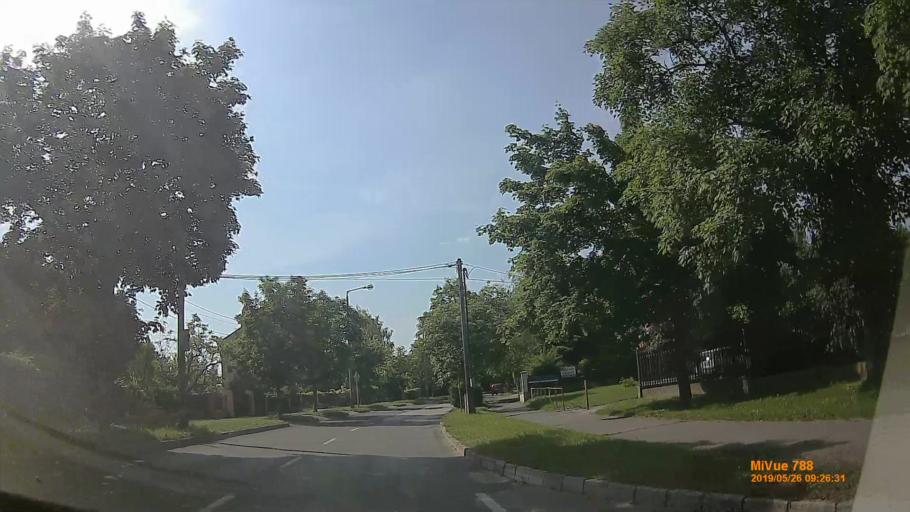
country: HU
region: Veszprem
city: Veszprem
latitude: 47.1015
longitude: 17.9249
